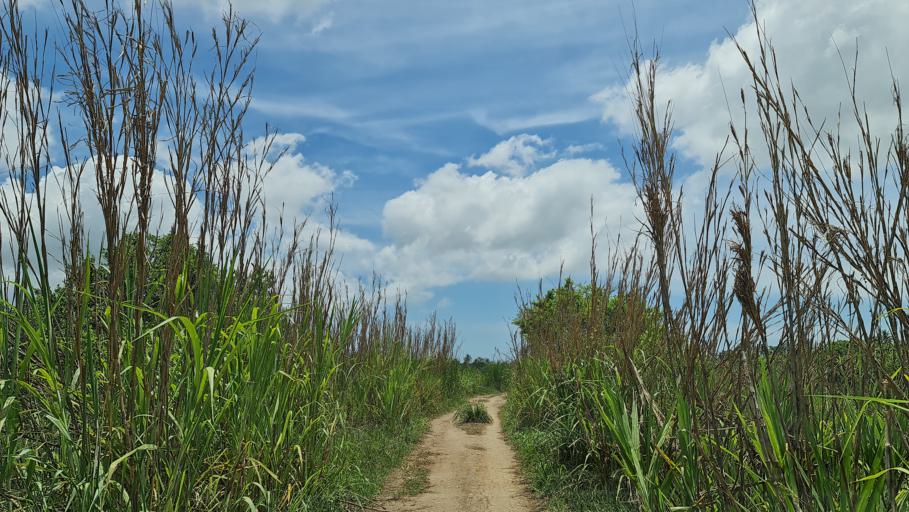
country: MZ
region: Zambezia
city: Quelimane
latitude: -17.5835
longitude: 37.3845
